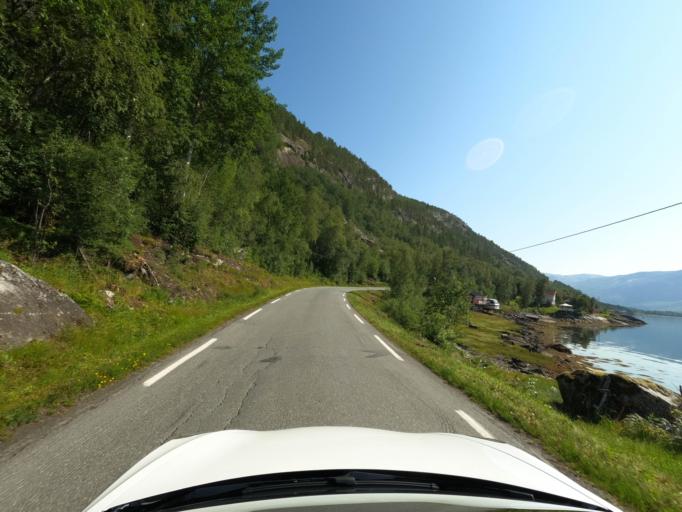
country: NO
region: Nordland
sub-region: Narvik
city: Narvik
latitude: 68.2746
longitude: 17.3975
